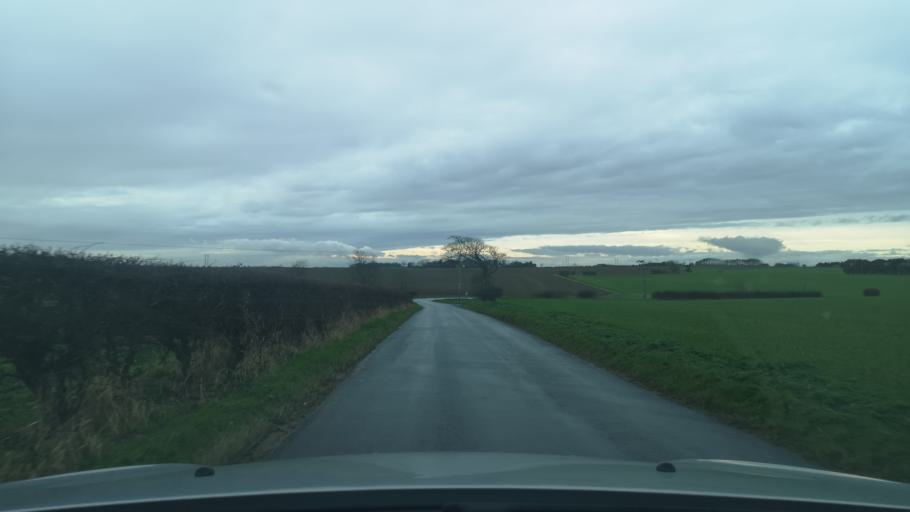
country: GB
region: England
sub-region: East Riding of Yorkshire
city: Holmpton
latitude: 53.6779
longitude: 0.0811
